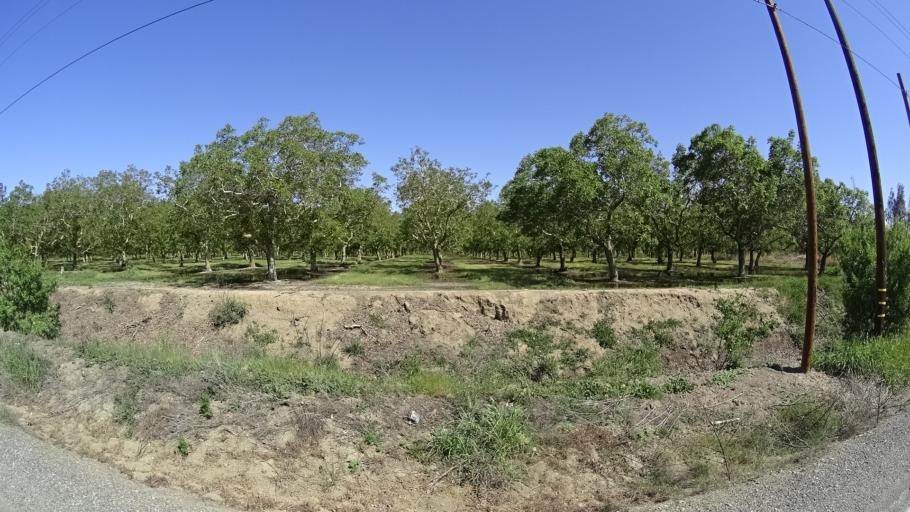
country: US
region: California
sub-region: Glenn County
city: Orland
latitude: 39.7105
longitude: -122.1257
